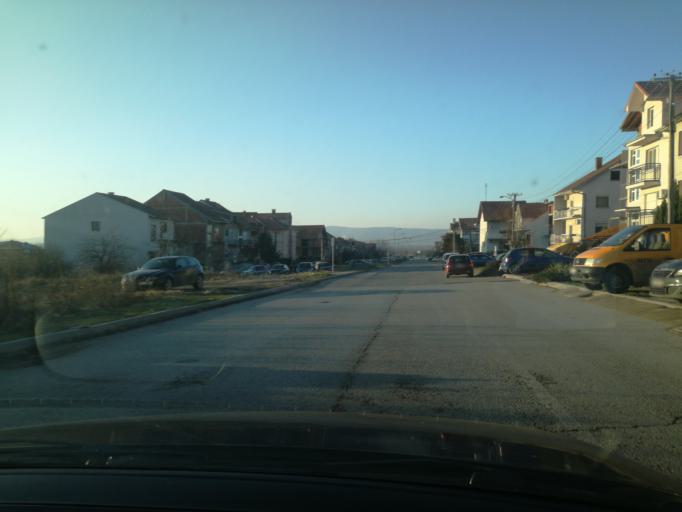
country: RS
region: Central Serbia
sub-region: Nisavski Okrug
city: Nis
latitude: 43.3083
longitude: 21.8629
